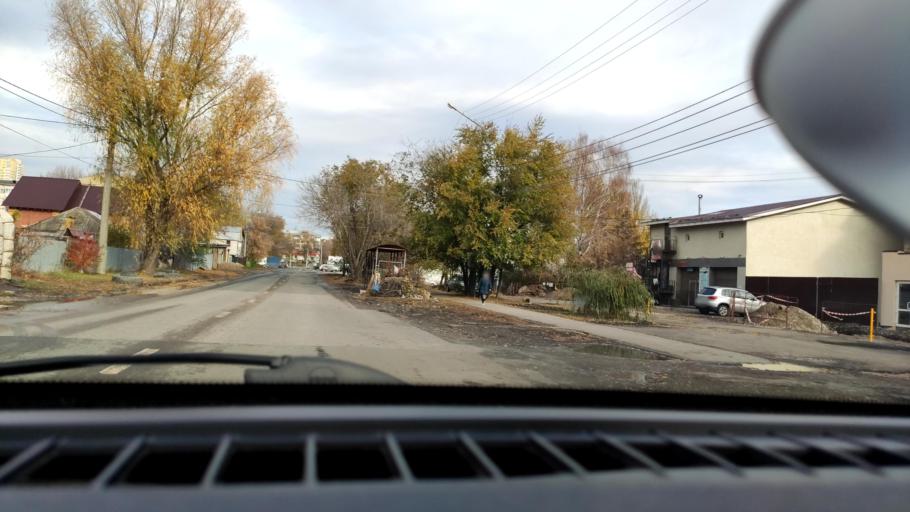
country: RU
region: Samara
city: Samara
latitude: 53.1984
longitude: 50.1986
